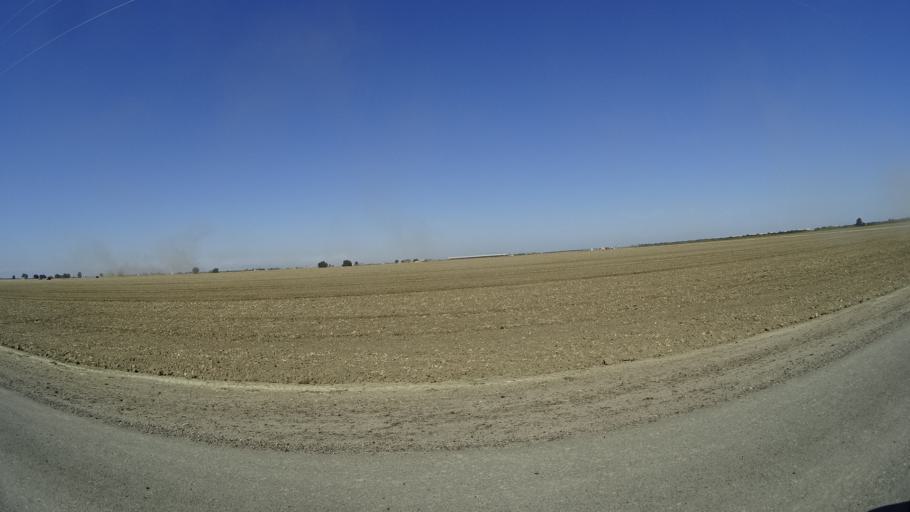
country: US
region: California
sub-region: Kings County
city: Home Garden
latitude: 36.2379
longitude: -119.5562
